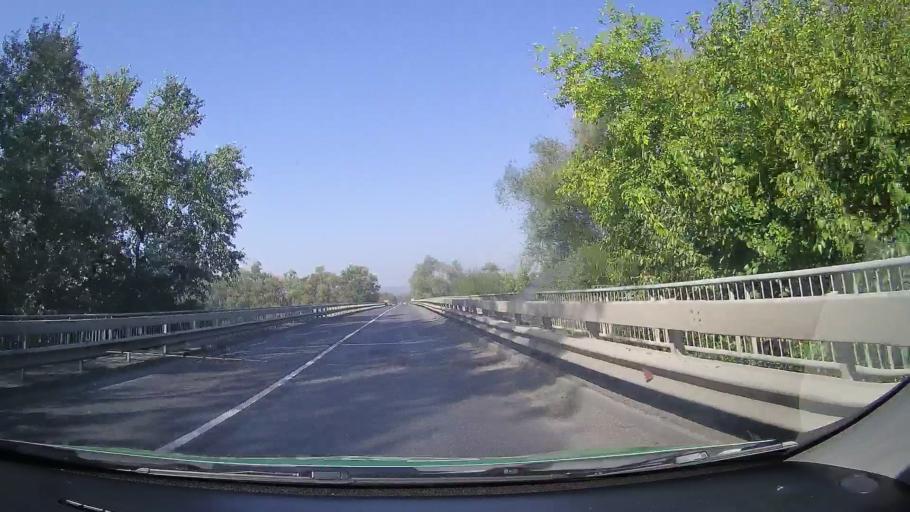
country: RO
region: Hunedoara
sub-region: Comuna Ilia
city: Ilia
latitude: 45.9240
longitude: 22.6691
